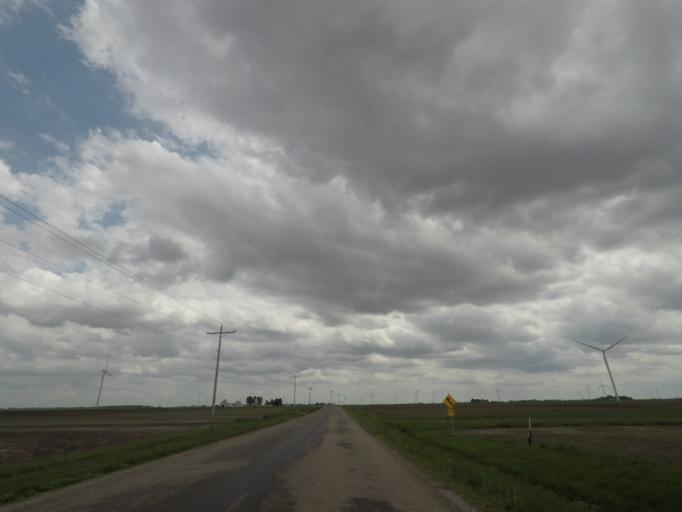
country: US
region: Illinois
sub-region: Macon County
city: Warrensburg
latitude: 40.0520
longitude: -89.0859
